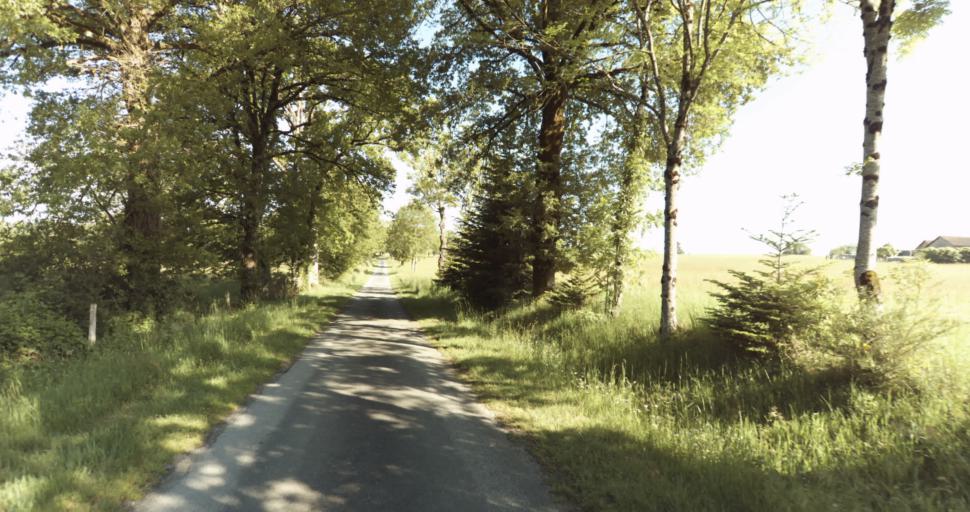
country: FR
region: Limousin
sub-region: Departement de la Haute-Vienne
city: Bosmie-l'Aiguille
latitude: 45.7262
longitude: 1.2379
